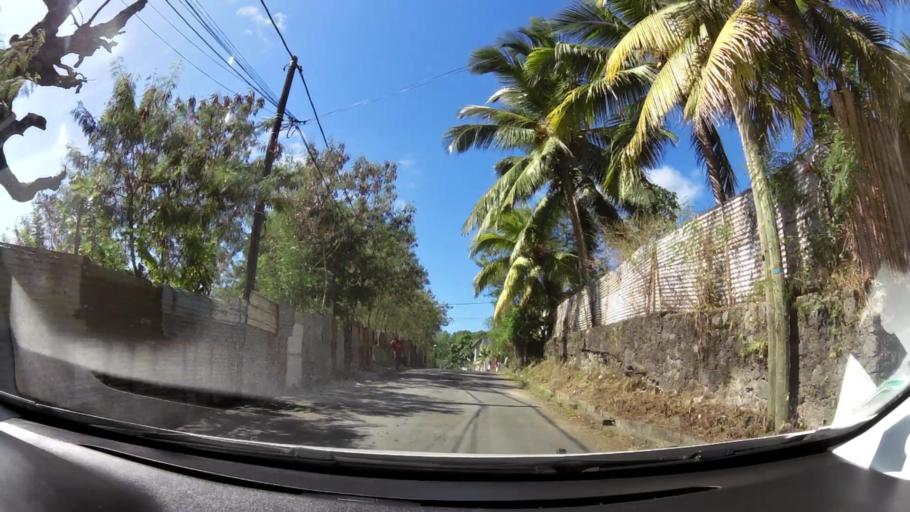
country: YT
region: Pamandzi
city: Pamandzi
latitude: -12.7871
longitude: 45.2794
